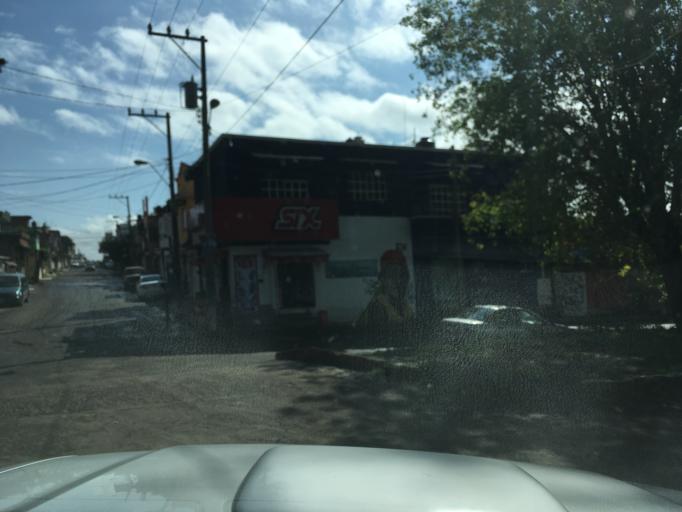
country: MX
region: Michoacan
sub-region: Tarimbaro
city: Fraccionamiento Metropolis II
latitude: 19.7216
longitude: -101.2319
